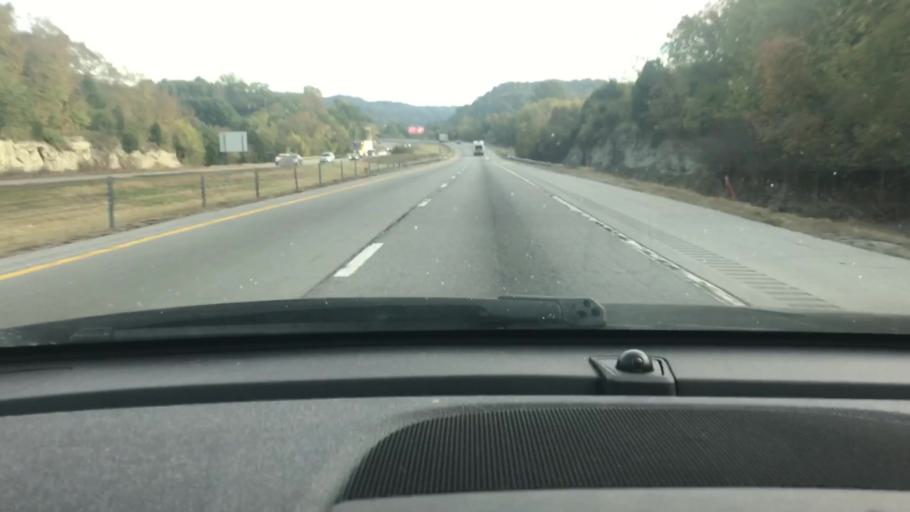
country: US
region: Tennessee
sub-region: Sumner County
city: Millersville
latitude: 36.3654
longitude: -86.7154
